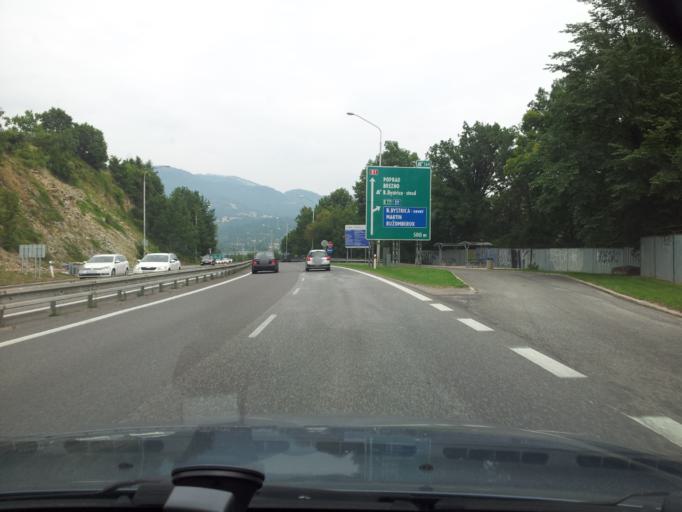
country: SK
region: Banskobystricky
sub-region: Okres Banska Bystrica
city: Banska Bystrica
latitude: 48.7422
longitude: 19.1373
